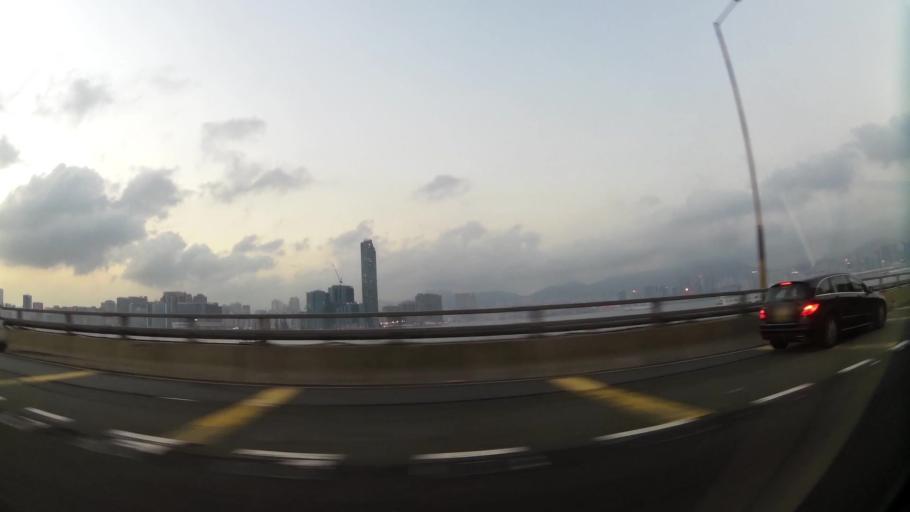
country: HK
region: Wanchai
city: Wan Chai
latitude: 22.2932
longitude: 114.1961
